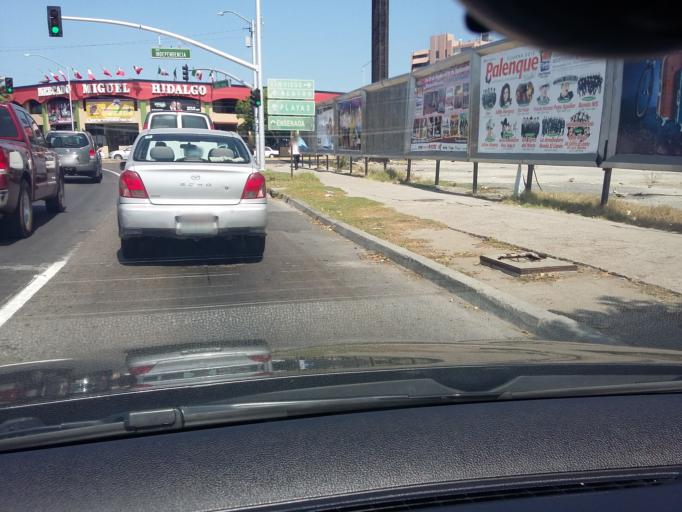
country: MX
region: Baja California
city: Tijuana
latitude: 32.5262
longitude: -117.0247
